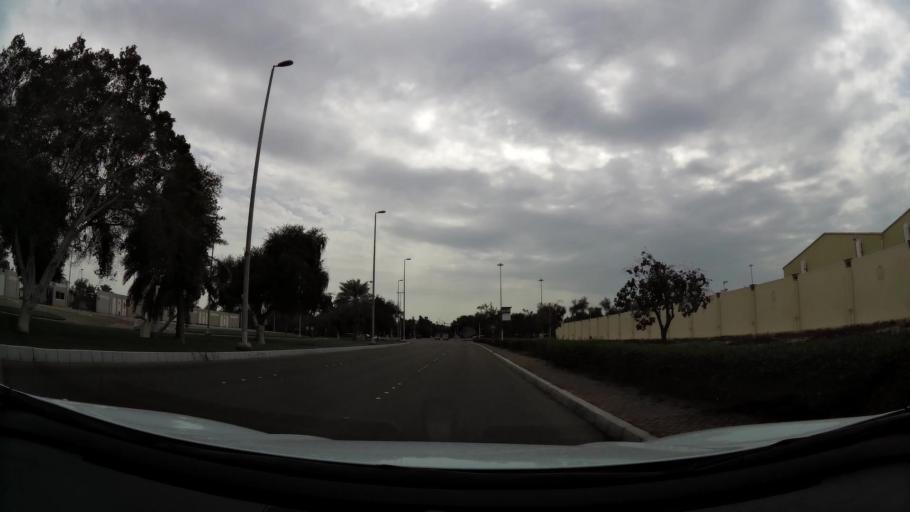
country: AE
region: Abu Dhabi
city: Abu Dhabi
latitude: 24.4321
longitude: 54.4200
